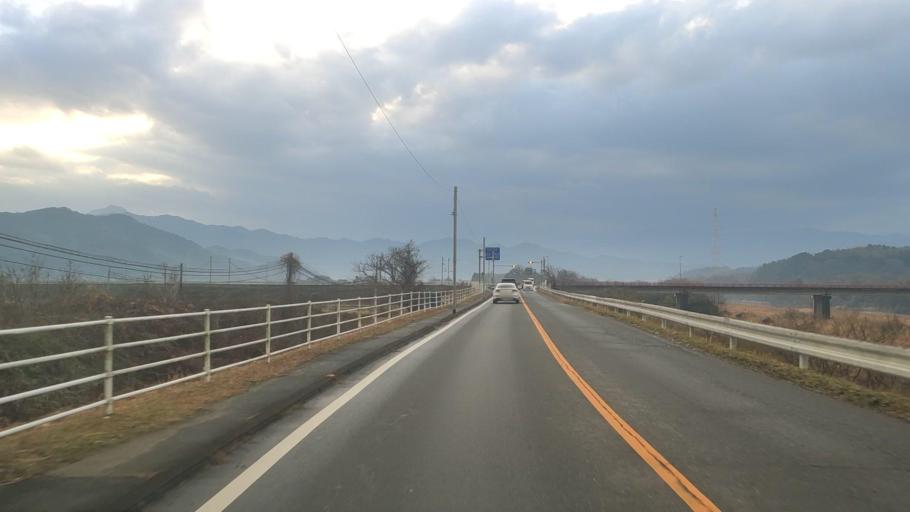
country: JP
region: Kumamoto
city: Uto
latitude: 32.6945
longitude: 130.7892
